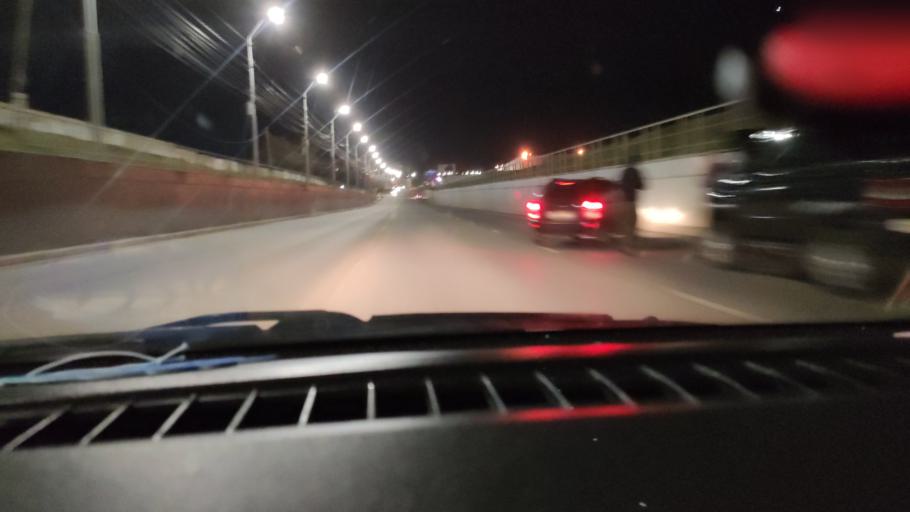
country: RU
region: Saratov
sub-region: Saratovskiy Rayon
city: Saratov
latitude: 51.5577
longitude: 46.0596
